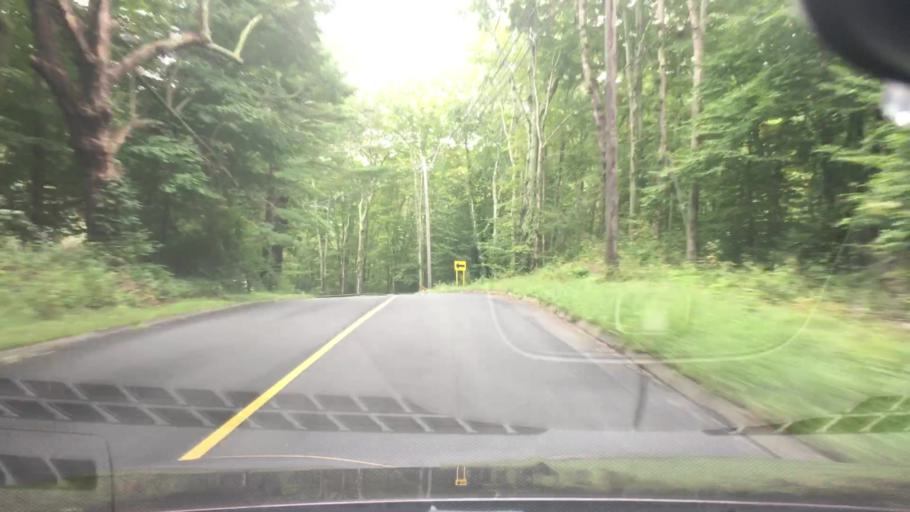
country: US
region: Connecticut
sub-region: New Haven County
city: Madison
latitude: 41.3253
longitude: -72.5928
